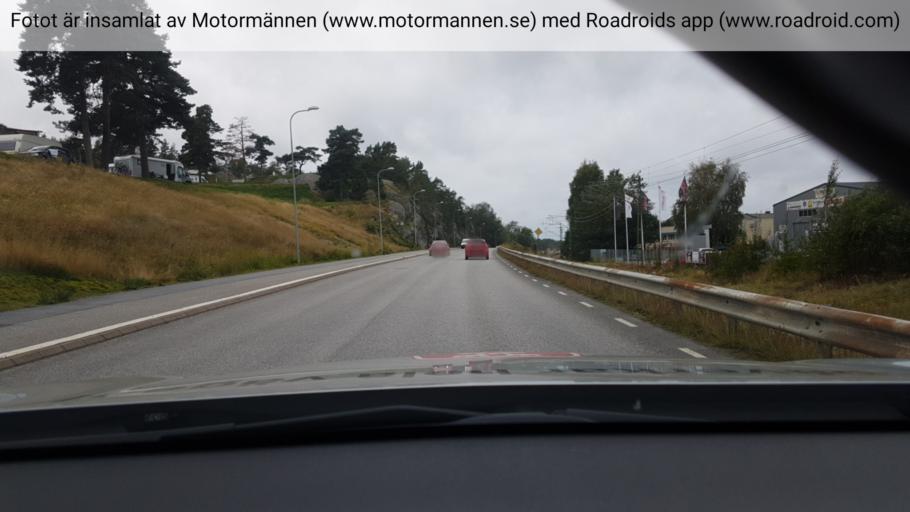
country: SE
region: Vaestra Goetaland
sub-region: Stromstads Kommun
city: Stroemstad
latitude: 58.9307
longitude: 11.1801
